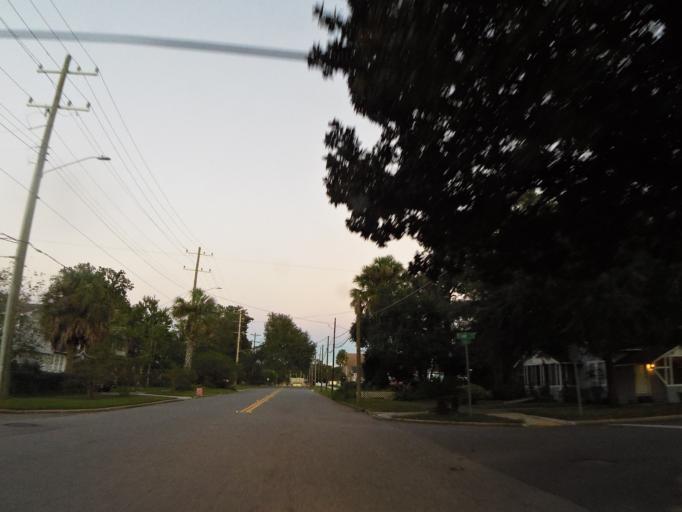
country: US
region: Florida
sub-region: Duval County
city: Jacksonville
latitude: 30.2883
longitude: -81.7181
